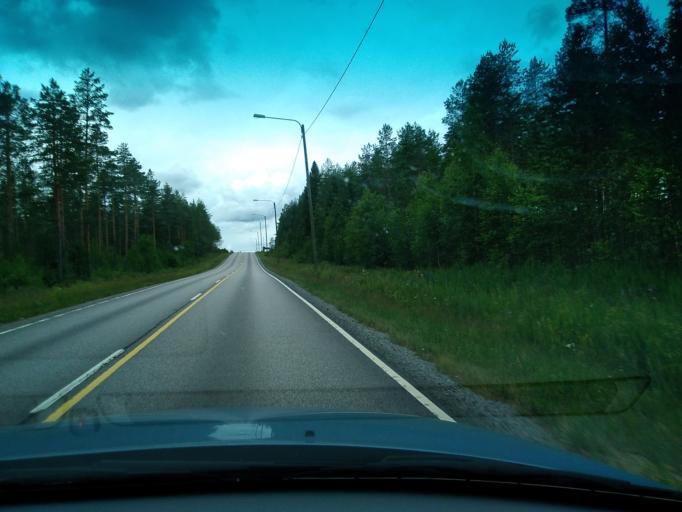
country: FI
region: Central Finland
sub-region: Saarijaervi-Viitasaari
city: Pylkoenmaeki
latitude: 62.6391
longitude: 24.8298
